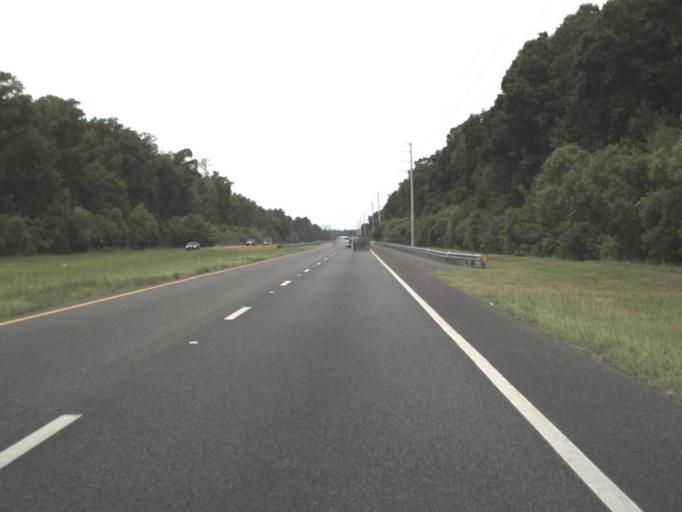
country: US
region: Florida
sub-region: Putnam County
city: Interlachen
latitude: 29.6288
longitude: -81.7645
